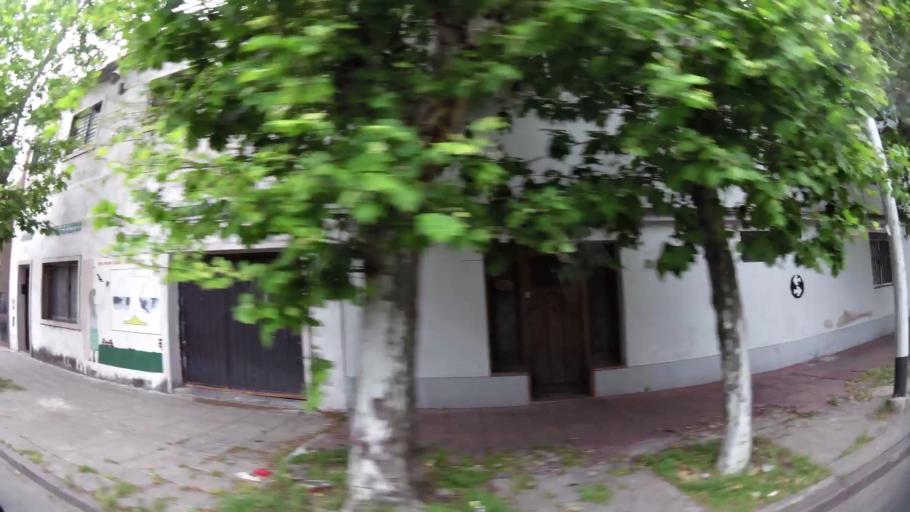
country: AR
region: Buenos Aires
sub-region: Partido de Lanus
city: Lanus
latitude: -34.6739
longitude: -58.3942
